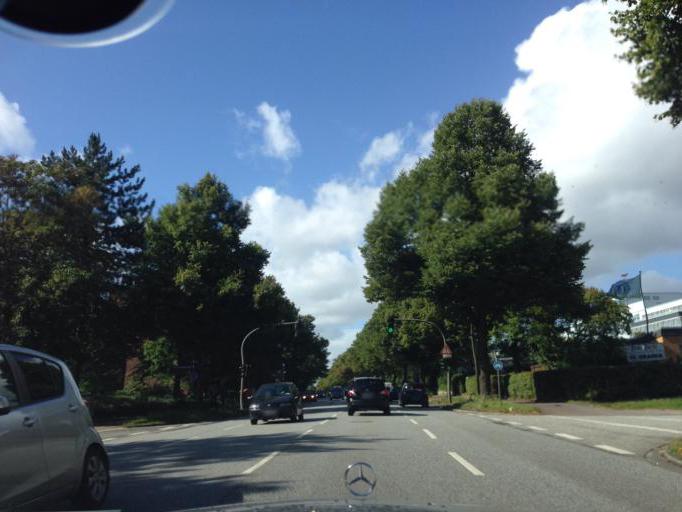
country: DE
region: Hamburg
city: Steilshoop
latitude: 53.5887
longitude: 10.0617
